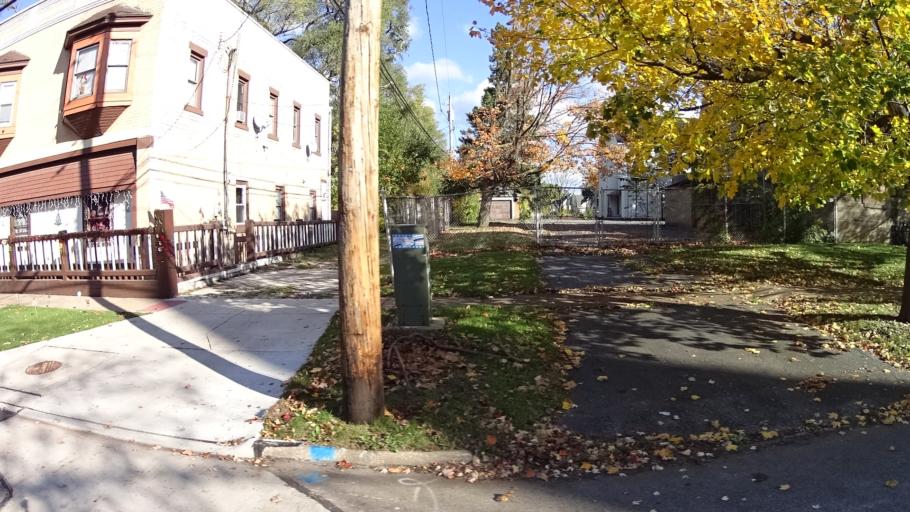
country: US
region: Ohio
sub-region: Lorain County
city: Lorain
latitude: 41.4427
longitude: -82.1413
